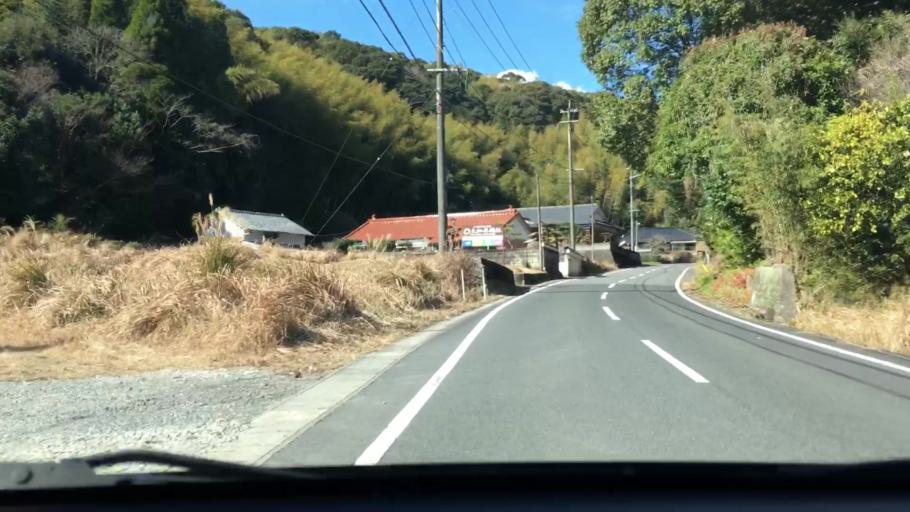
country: JP
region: Kagoshima
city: Ijuin
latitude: 31.7102
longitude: 130.4392
